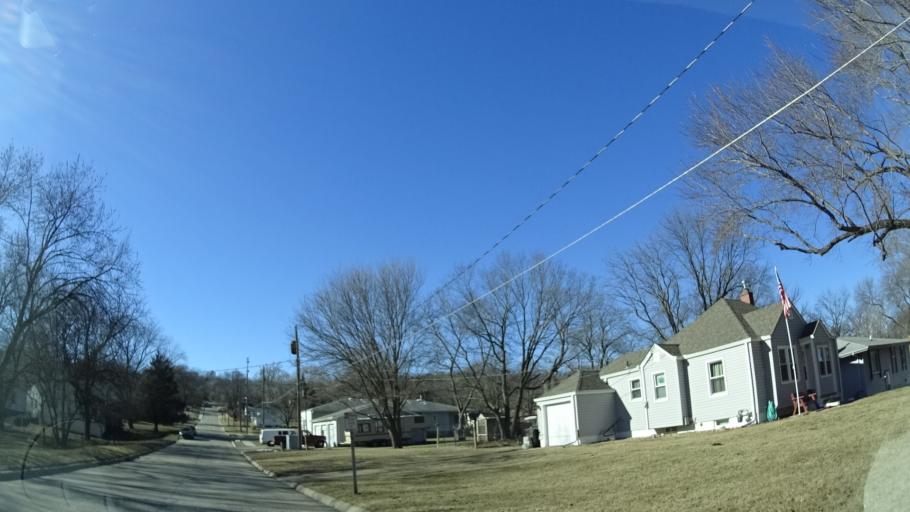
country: US
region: Nebraska
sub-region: Sarpy County
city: Bellevue
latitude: 41.1447
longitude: -95.8896
